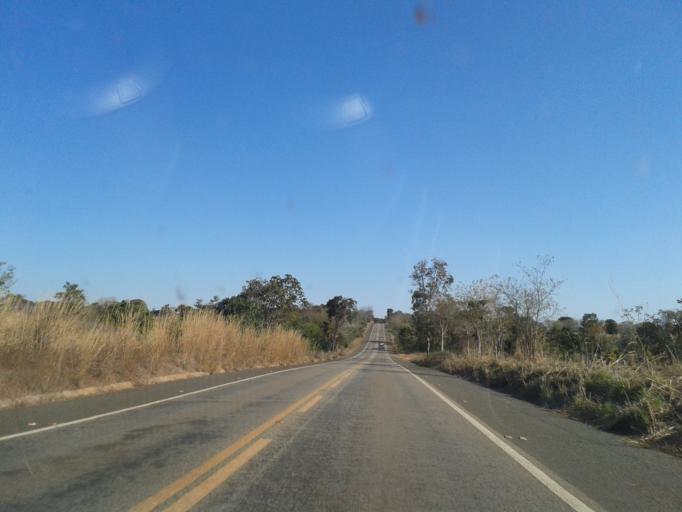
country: BR
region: Goias
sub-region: Mozarlandia
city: Mozarlandia
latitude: -15.0743
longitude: -50.6198
